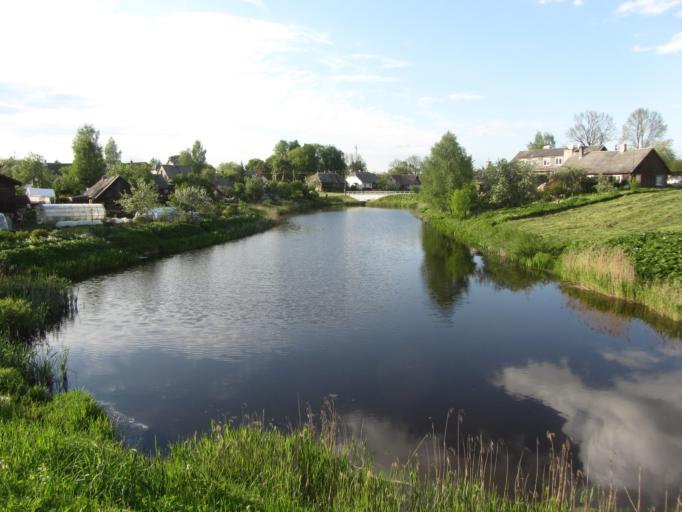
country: LT
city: Sirvintos
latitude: 55.0446
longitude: 24.9508
